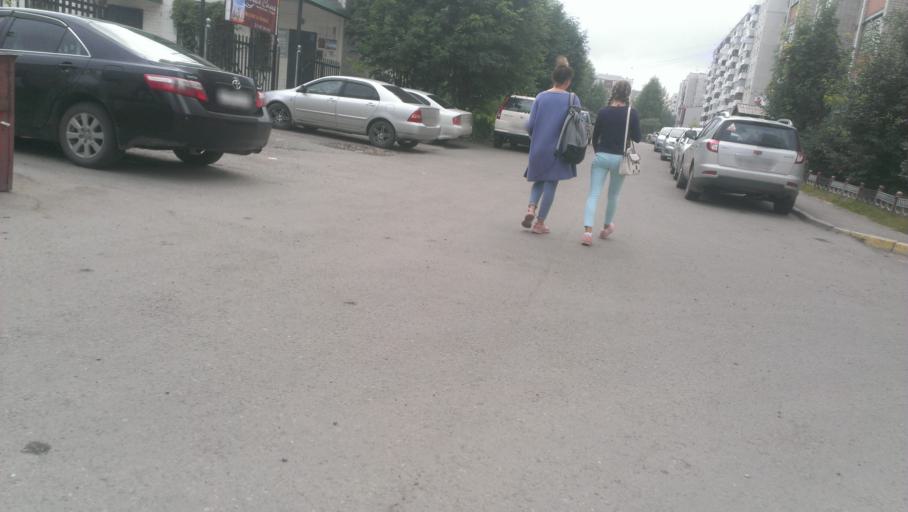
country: RU
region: Altai Krai
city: Novosilikatnyy
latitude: 53.3330
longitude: 83.6840
